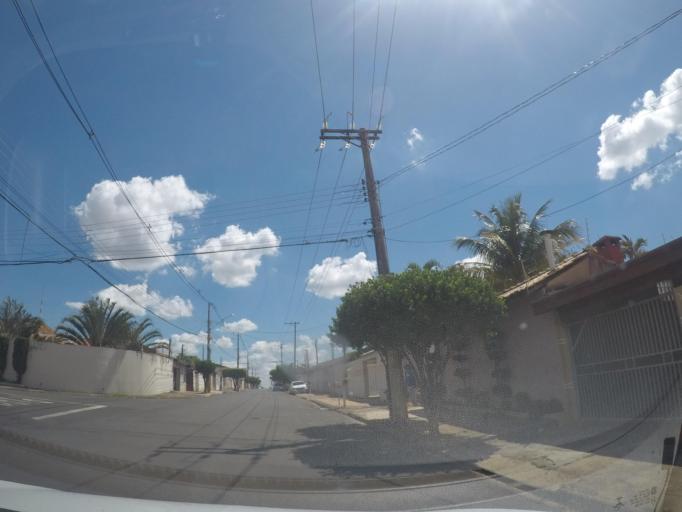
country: BR
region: Sao Paulo
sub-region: Sumare
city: Sumare
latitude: -22.8282
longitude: -47.2788
